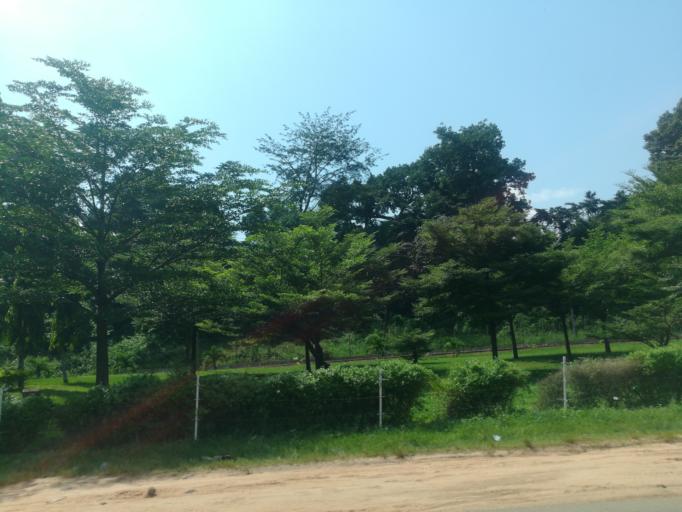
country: NG
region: Oyo
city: Moniya
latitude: 7.4943
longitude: 3.9147
